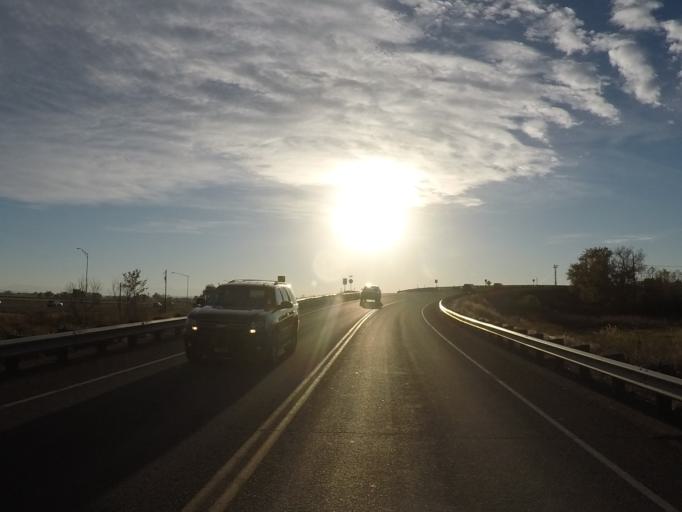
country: US
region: Montana
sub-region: Yellowstone County
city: Laurel
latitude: 45.6825
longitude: -108.7101
